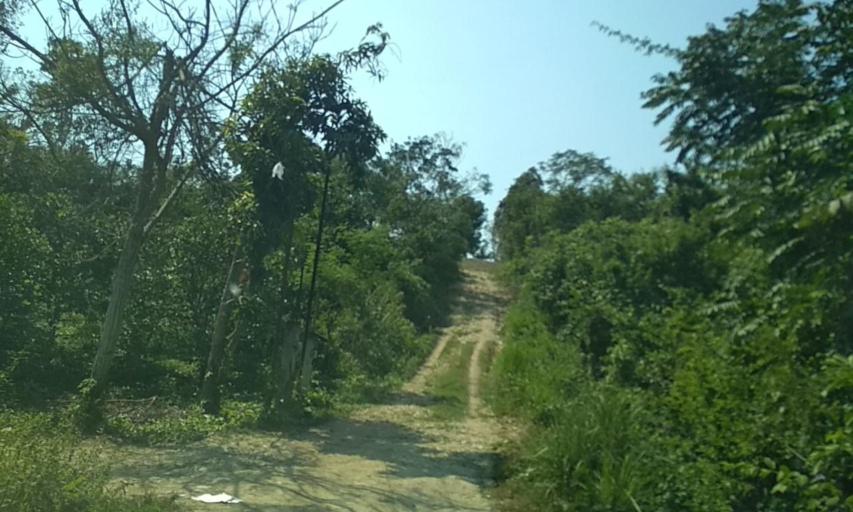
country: MX
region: Veracruz
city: Gutierrez Zamora
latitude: 20.4241
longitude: -97.1957
